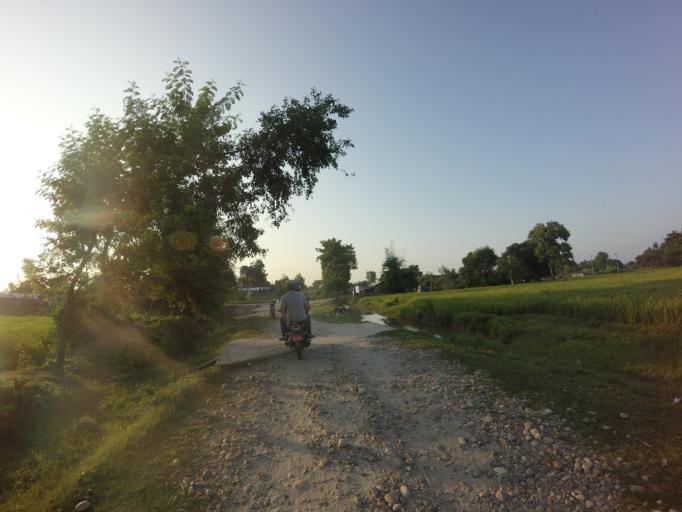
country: NP
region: Far Western
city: Tikapur
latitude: 28.4523
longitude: 81.0725
